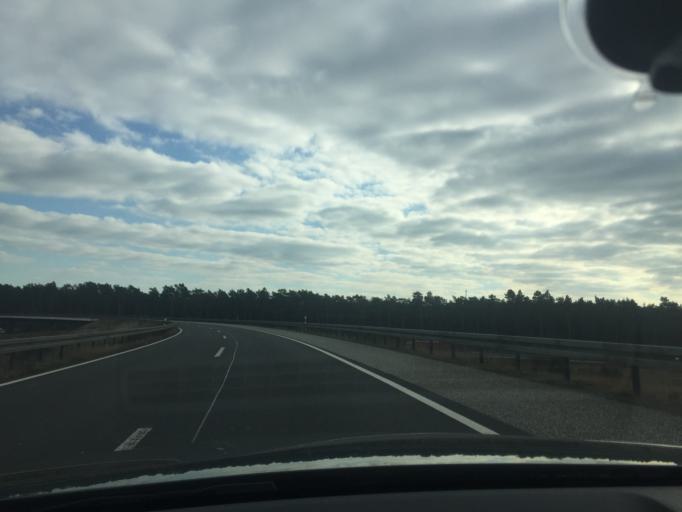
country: DE
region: Brandenburg
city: Erkner
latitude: 52.3252
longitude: 13.7491
